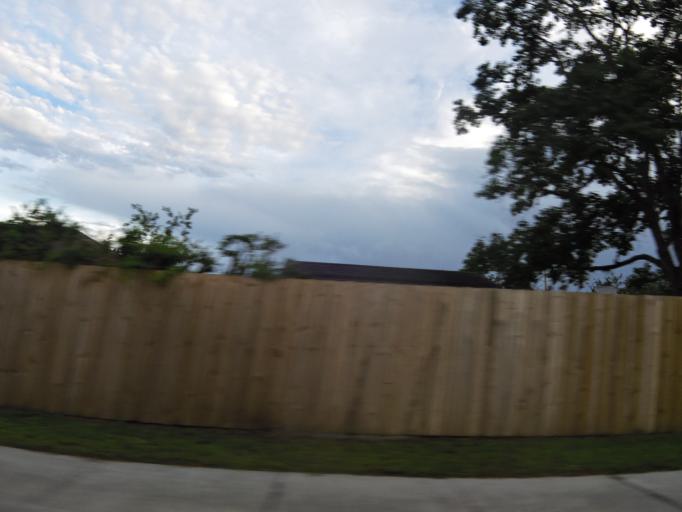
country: US
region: Florida
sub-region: Clay County
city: Bellair-Meadowbrook Terrace
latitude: 30.3020
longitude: -81.8196
